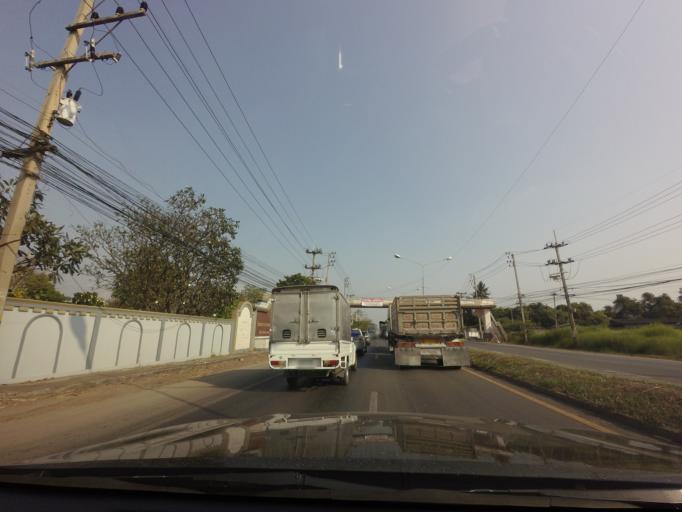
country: TH
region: Kanchanaburi
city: Tha Maka
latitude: 13.8671
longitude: 99.8237
